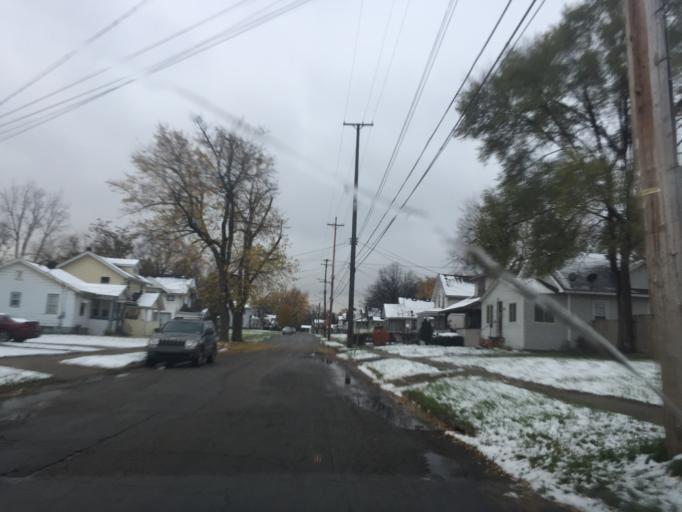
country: US
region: Michigan
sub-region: Oakland County
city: Pontiac
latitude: 42.6377
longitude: -83.2785
